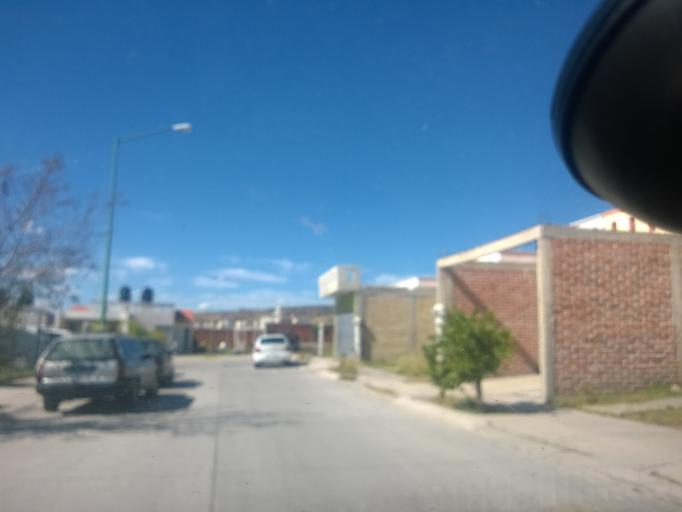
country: MX
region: Guanajuato
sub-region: Leon
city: La Ermita
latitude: 21.1572
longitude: -101.7467
